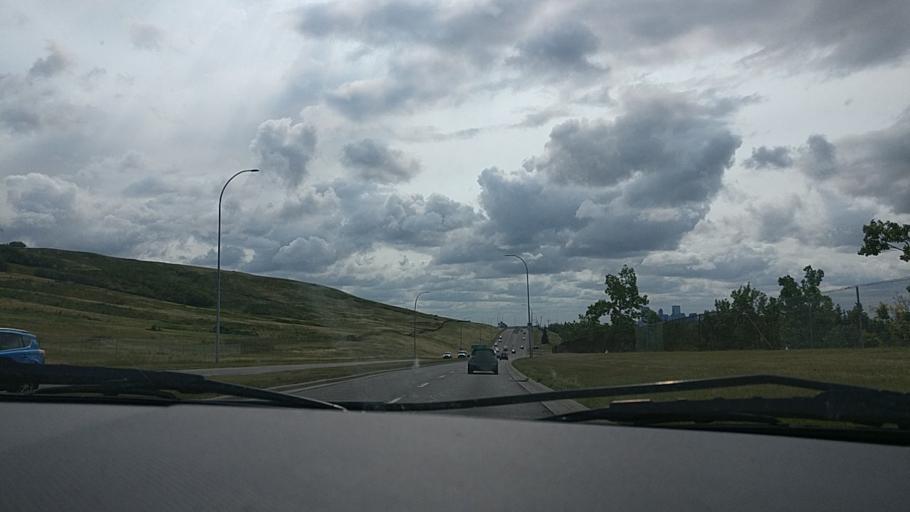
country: CA
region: Alberta
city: Calgary
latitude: 51.0991
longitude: -114.1202
